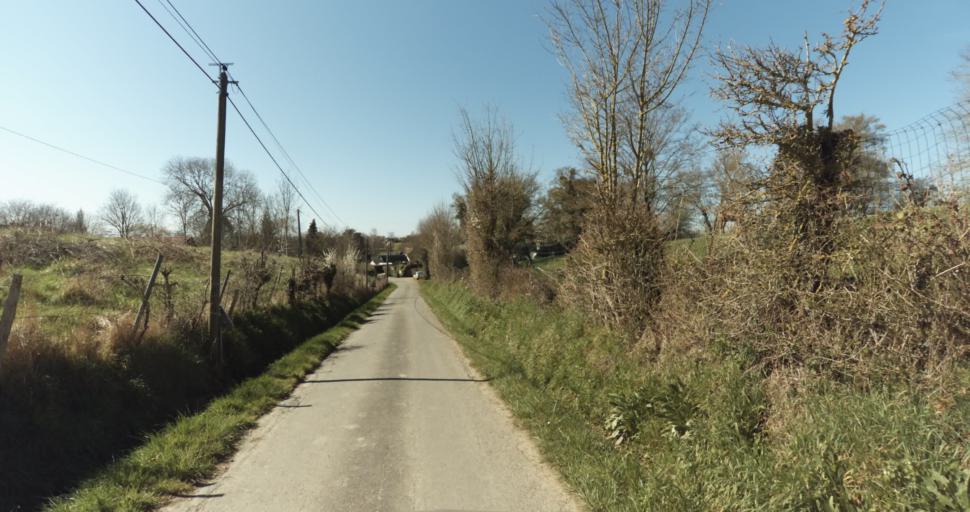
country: FR
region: Lower Normandy
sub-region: Departement du Calvados
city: Saint-Pierre-sur-Dives
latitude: 49.0536
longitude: -0.0214
